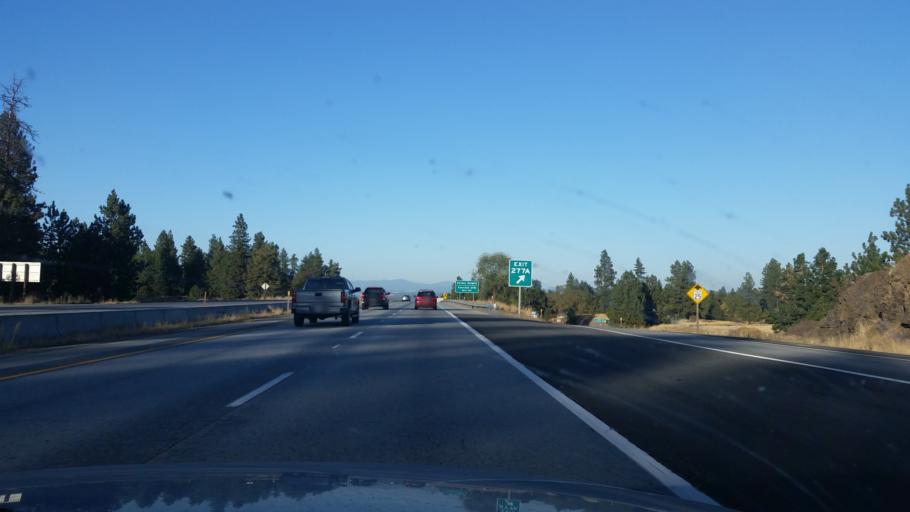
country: US
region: Washington
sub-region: Spokane County
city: Spokane
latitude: 47.6295
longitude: -117.4866
